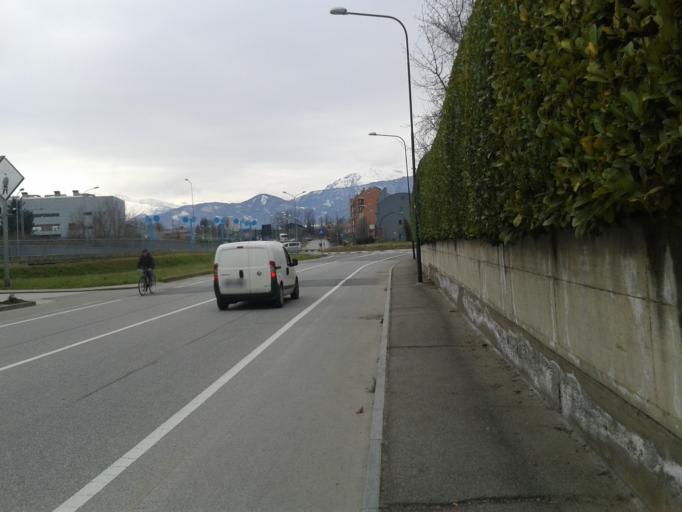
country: IT
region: Piedmont
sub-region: Provincia di Torino
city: Pinerolo
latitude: 44.8932
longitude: 7.3514
